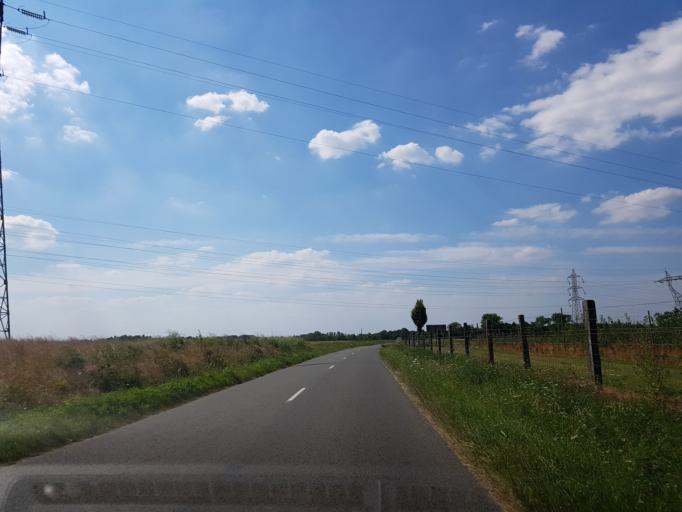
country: FR
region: Nord-Pas-de-Calais
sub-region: Departement du Nord
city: Roeulx
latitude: 50.3190
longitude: 3.3229
